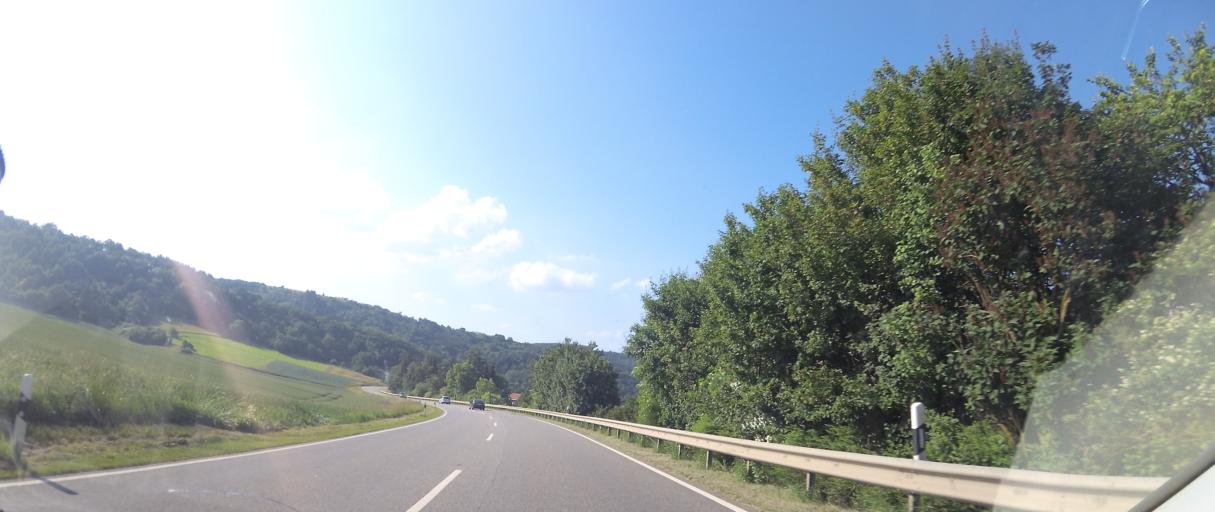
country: DE
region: Rheinland-Pfalz
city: Meisenheim
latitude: 49.7085
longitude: 7.6621
